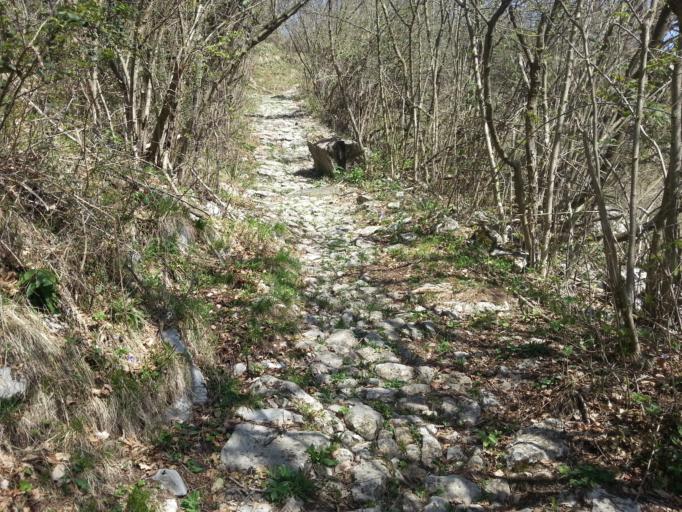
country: IT
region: Lombardy
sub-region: Provincia di Como
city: Tremezzo
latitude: 45.9982
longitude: 9.2086
